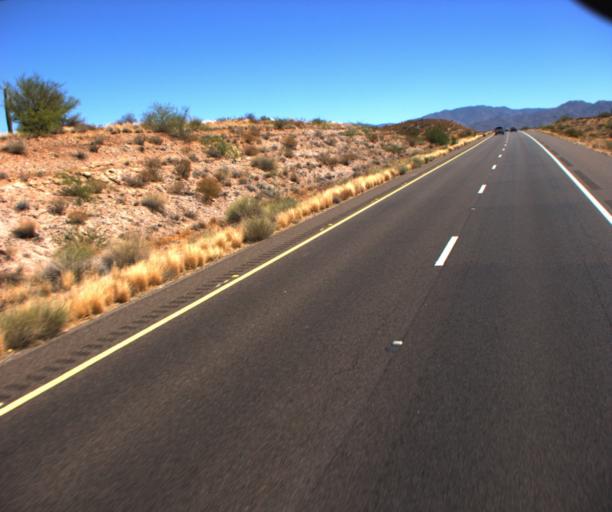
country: US
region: Arizona
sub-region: Maricopa County
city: Rio Verde
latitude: 33.6339
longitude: -111.5495
